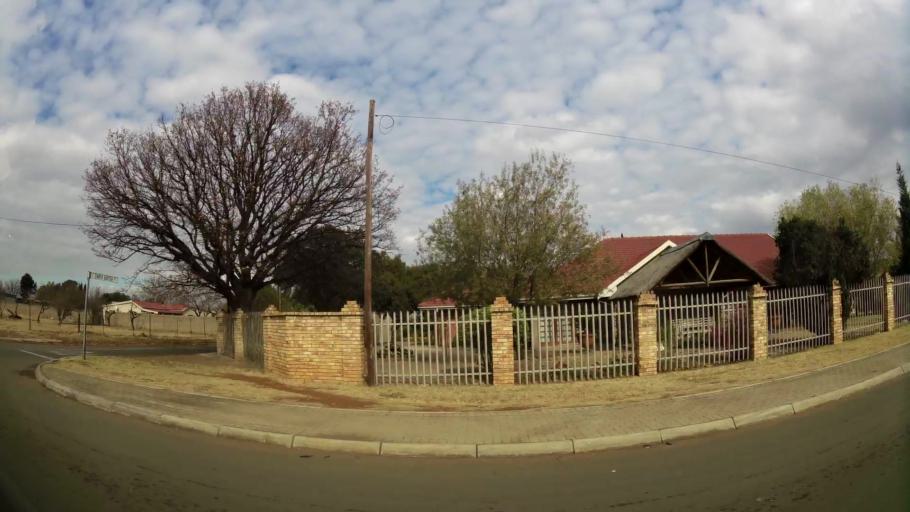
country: ZA
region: Gauteng
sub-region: Sedibeng District Municipality
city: Meyerton
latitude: -26.5997
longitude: 28.0438
